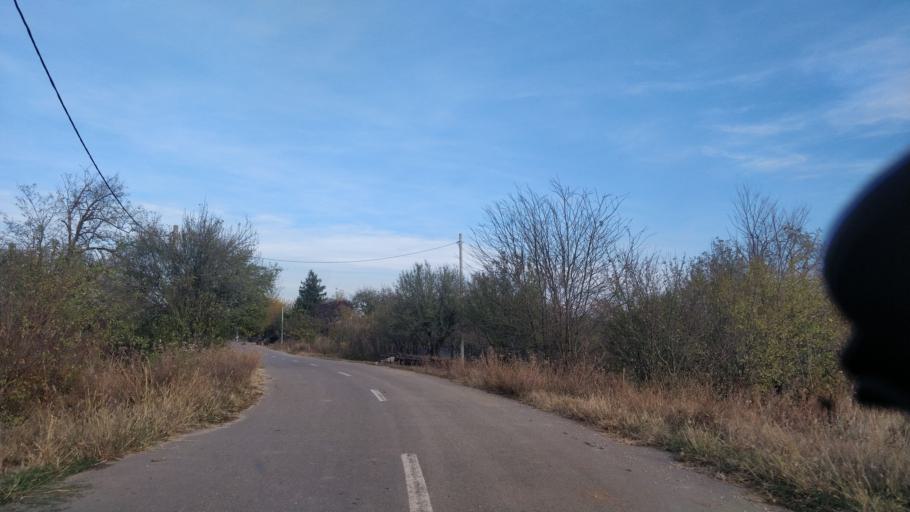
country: RO
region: Giurgiu
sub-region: Comuna Bucsani
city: Bucsani
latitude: 44.3346
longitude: 25.6399
